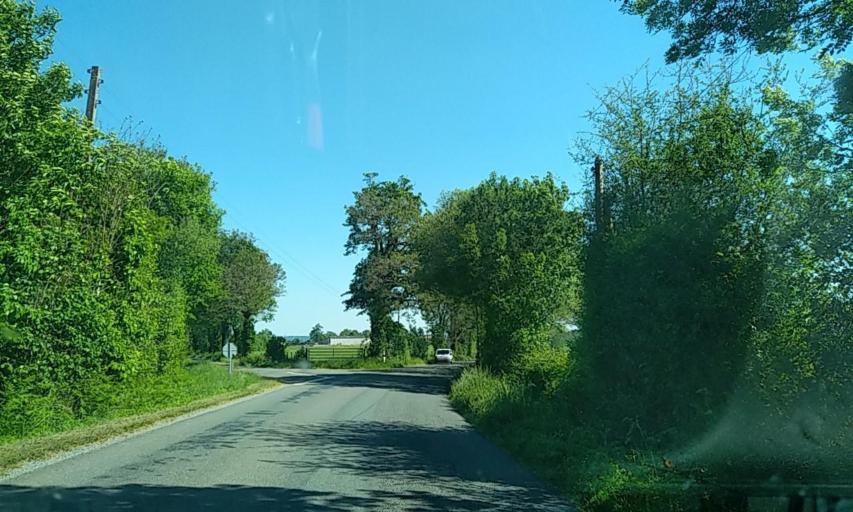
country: FR
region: Poitou-Charentes
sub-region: Departement des Deux-Sevres
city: Boisme
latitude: 46.7988
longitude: -0.4543
